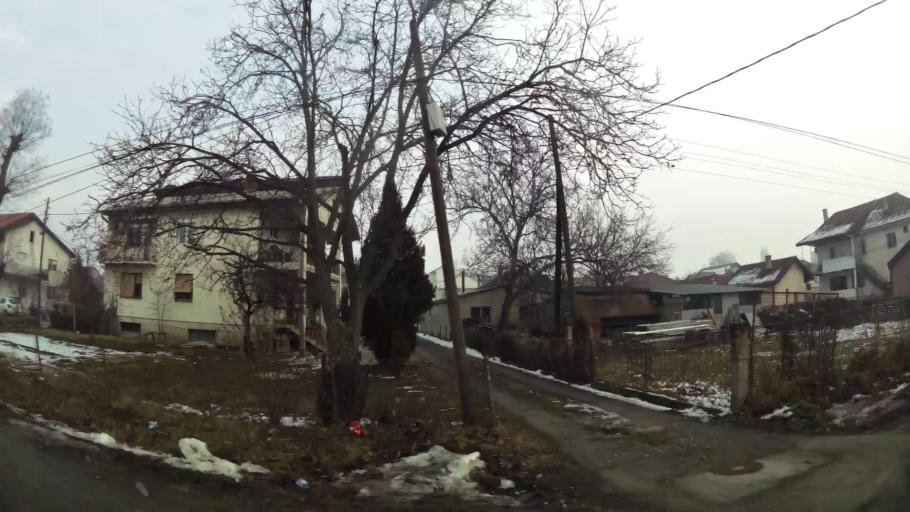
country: MK
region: Ilinden
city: Jurumleri
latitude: 41.9823
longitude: 21.5248
